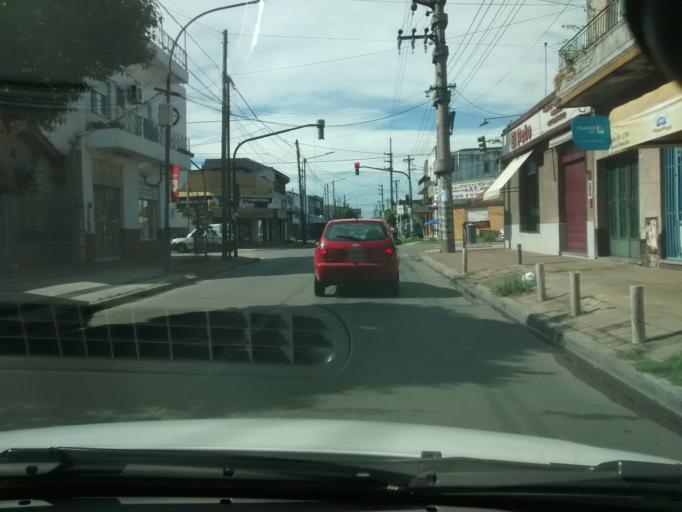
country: AR
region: Buenos Aires
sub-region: Partido de Moron
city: Moron
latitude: -34.6673
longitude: -58.6152
